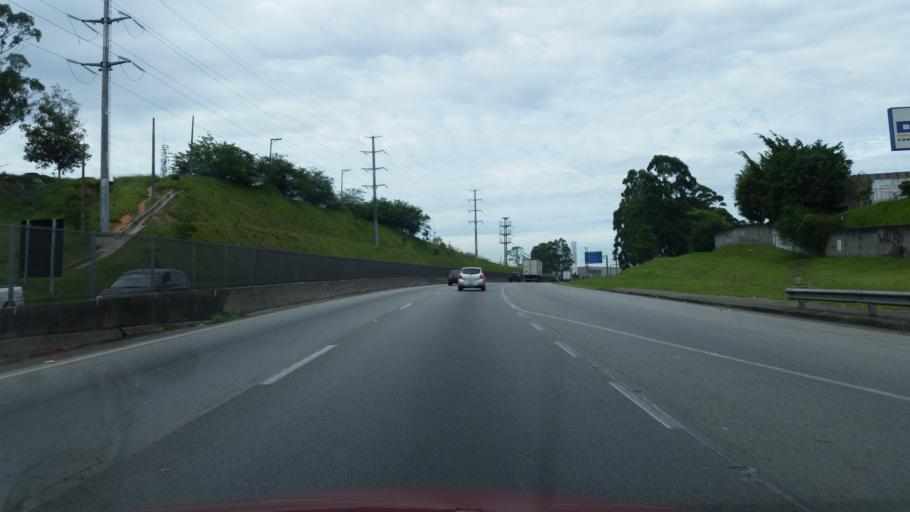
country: BR
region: Sao Paulo
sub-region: Taboao Da Serra
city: Taboao da Serra
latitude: -23.6334
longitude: -46.8234
